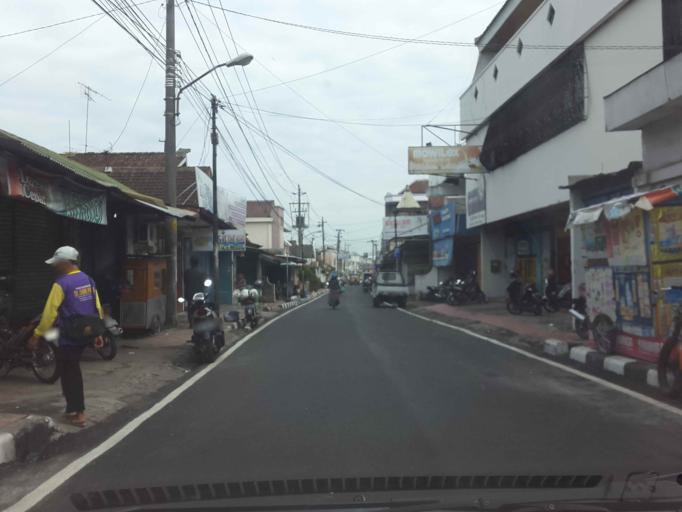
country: ID
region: Central Java
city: Salatiga
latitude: -7.3336
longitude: 110.5035
